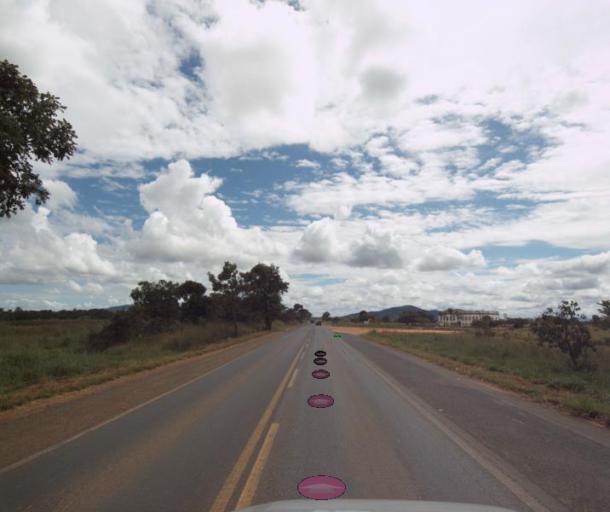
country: BR
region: Goias
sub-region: Uruacu
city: Uruacu
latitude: -14.4605
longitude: -49.1562
